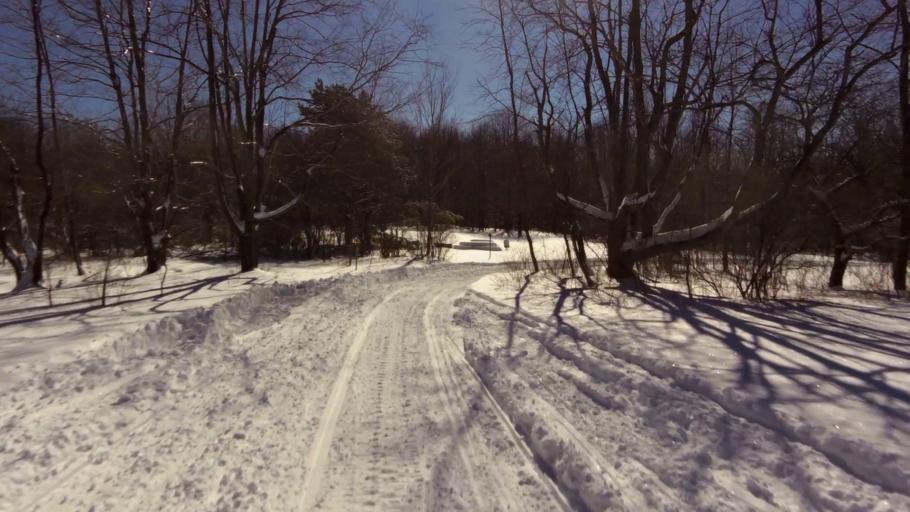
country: US
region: New York
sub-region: Chautauqua County
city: Mayville
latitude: 42.2364
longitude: -79.3902
